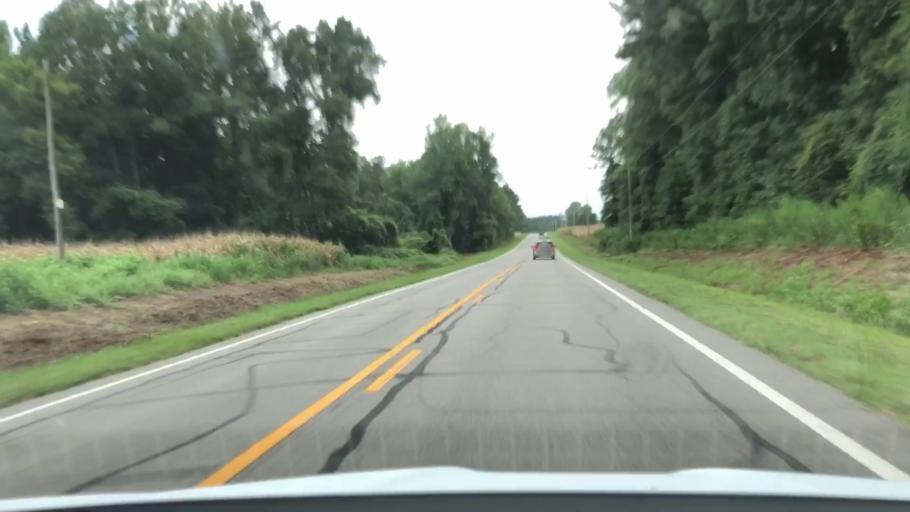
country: US
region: North Carolina
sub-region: Lenoir County
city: Kinston
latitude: 35.1664
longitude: -77.5571
